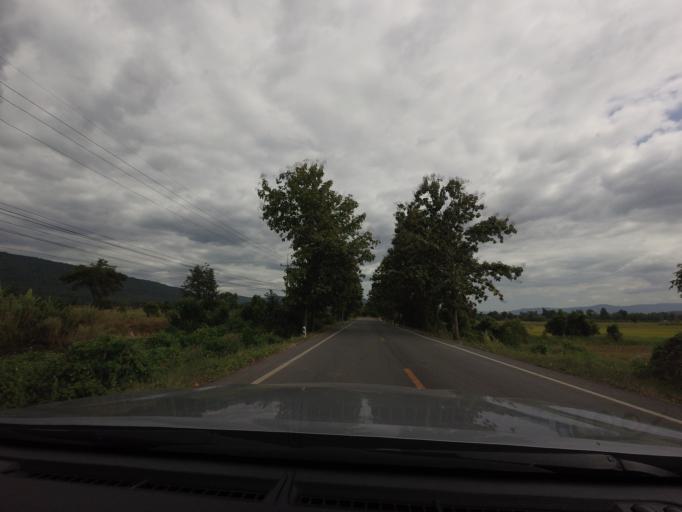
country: TH
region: Phitsanulok
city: Noen Maprang
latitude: 16.6930
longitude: 100.5506
